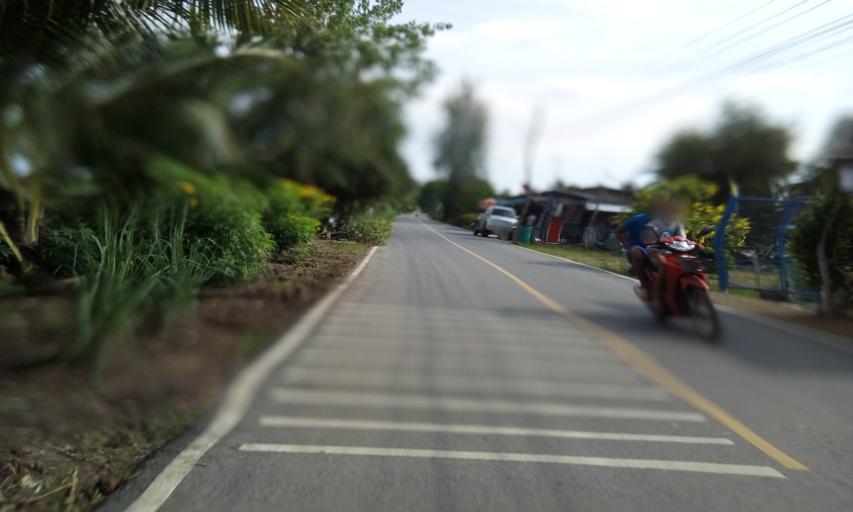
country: TH
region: Pathum Thani
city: Nong Suea
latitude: 14.1696
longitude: 100.8231
